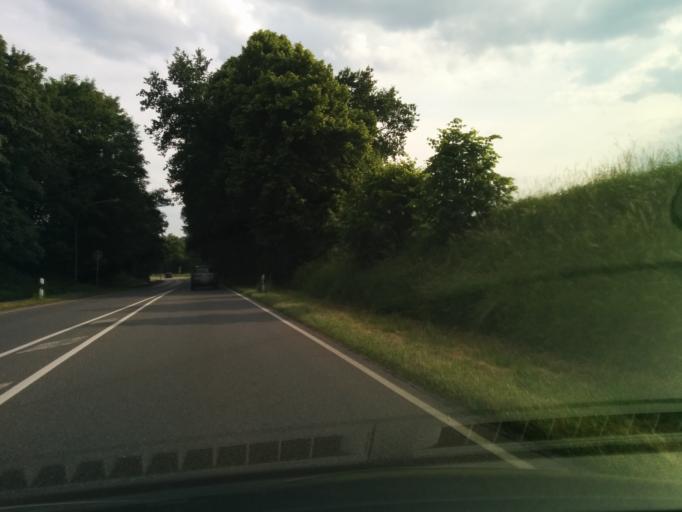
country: DE
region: Lower Saxony
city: Seevetal
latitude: 53.3987
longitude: 9.9768
